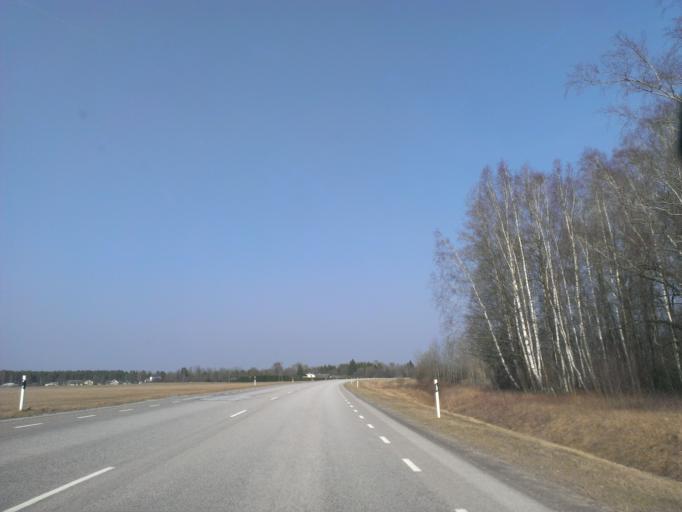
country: EE
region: Saare
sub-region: Orissaare vald
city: Orissaare
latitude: 58.4334
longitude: 22.7877
